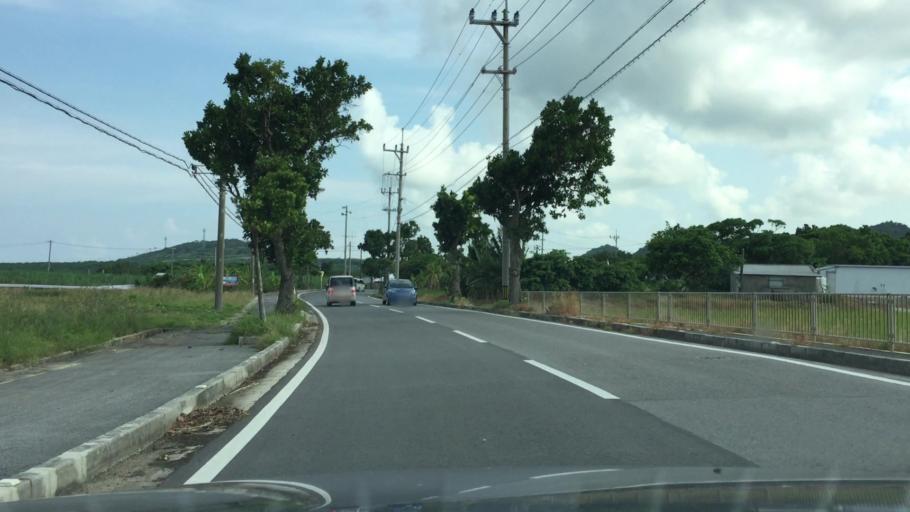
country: JP
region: Okinawa
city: Ishigaki
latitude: 24.4586
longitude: 124.2493
